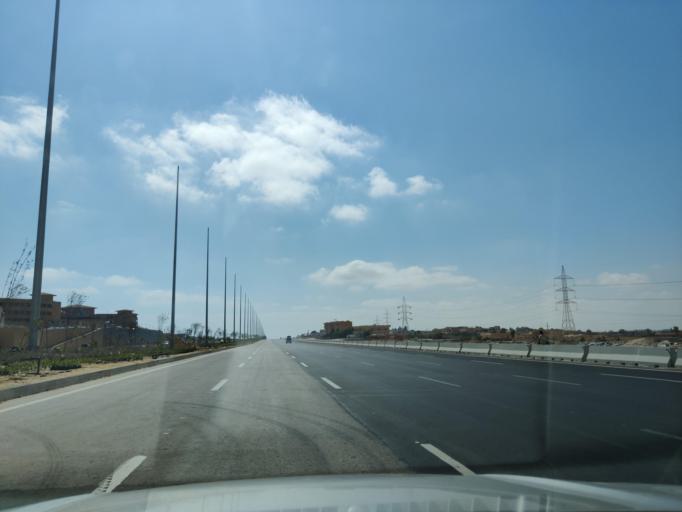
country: EG
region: Muhafazat Matruh
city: Al `Alamayn
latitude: 30.9932
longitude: 28.6676
